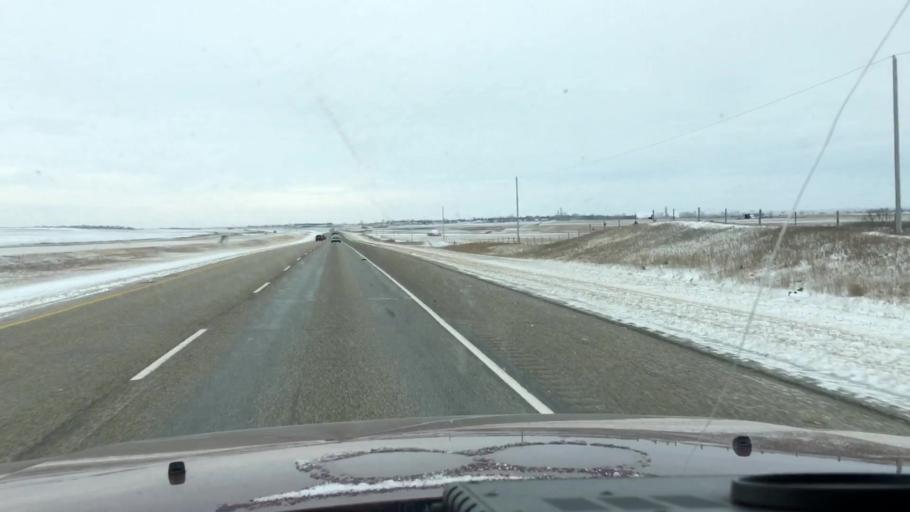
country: CA
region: Saskatchewan
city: Saskatoon
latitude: 51.6545
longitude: -106.4423
